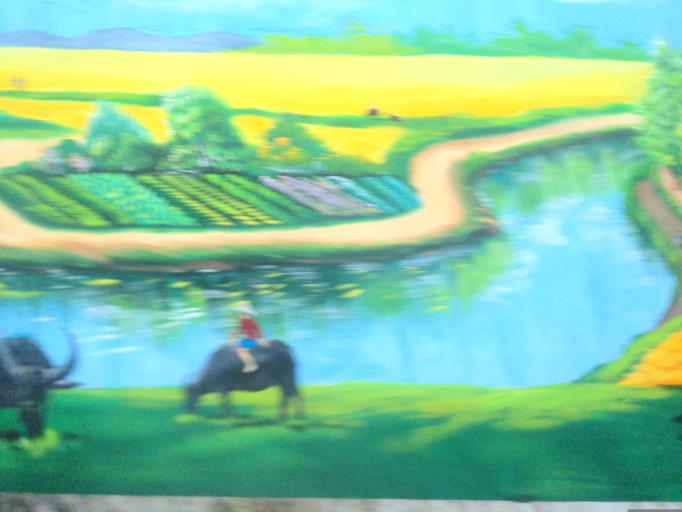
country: VN
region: Ninh Binh
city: Thi Tran Tam Diep
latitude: 20.2170
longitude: 105.9177
